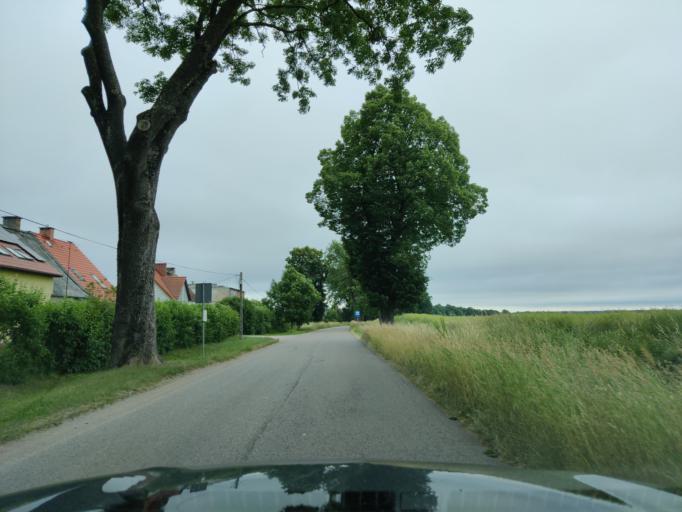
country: PL
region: Warmian-Masurian Voivodeship
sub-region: Powiat gizycki
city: Ryn
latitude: 53.9247
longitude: 21.5523
